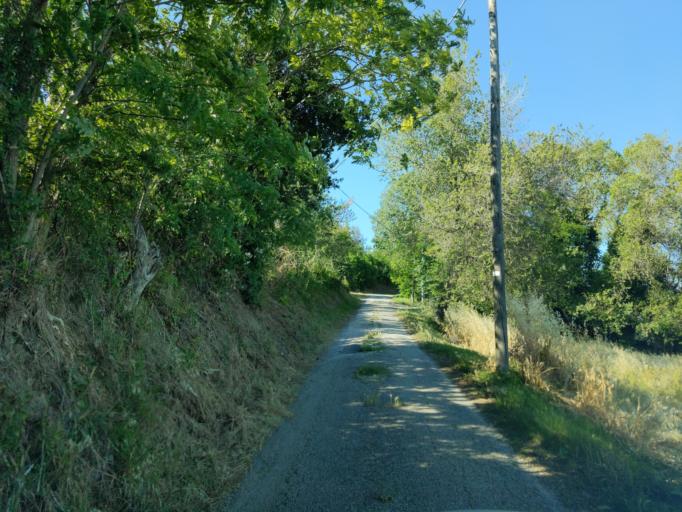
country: IT
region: The Marches
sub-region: Provincia di Pesaro e Urbino
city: Cuccurano
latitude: 43.8005
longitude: 12.9624
